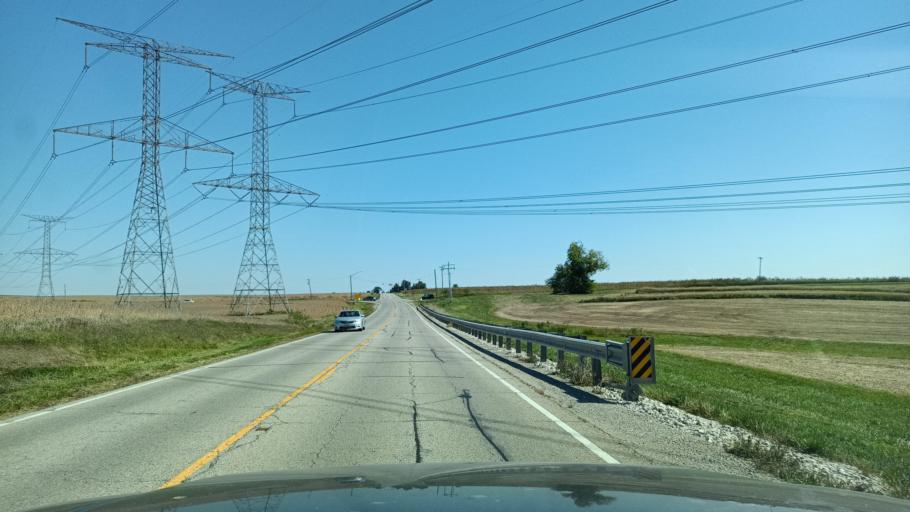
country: US
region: Illinois
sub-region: Tazewell County
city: Morton
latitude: 40.6139
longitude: -89.4058
